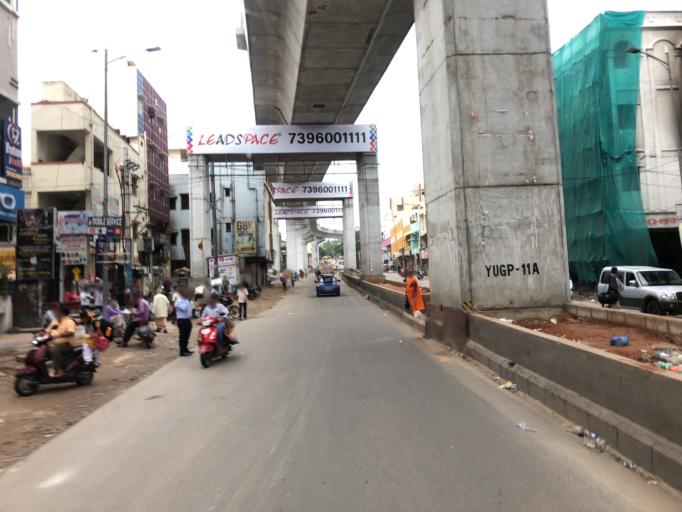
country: IN
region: Telangana
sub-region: Rangareddi
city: Kukatpalli
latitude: 17.4322
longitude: 78.4262
